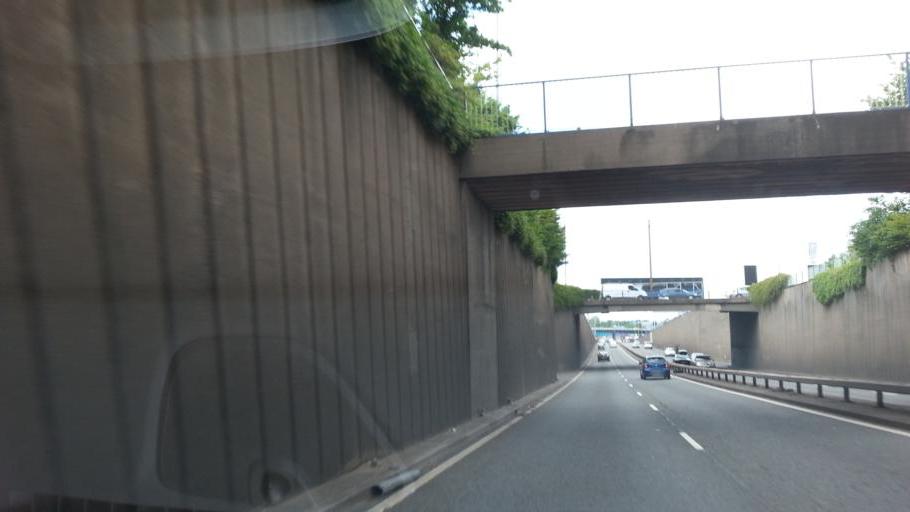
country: GB
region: England
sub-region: City and Borough of Birmingham
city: Birmingham
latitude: 52.4919
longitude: -1.8887
